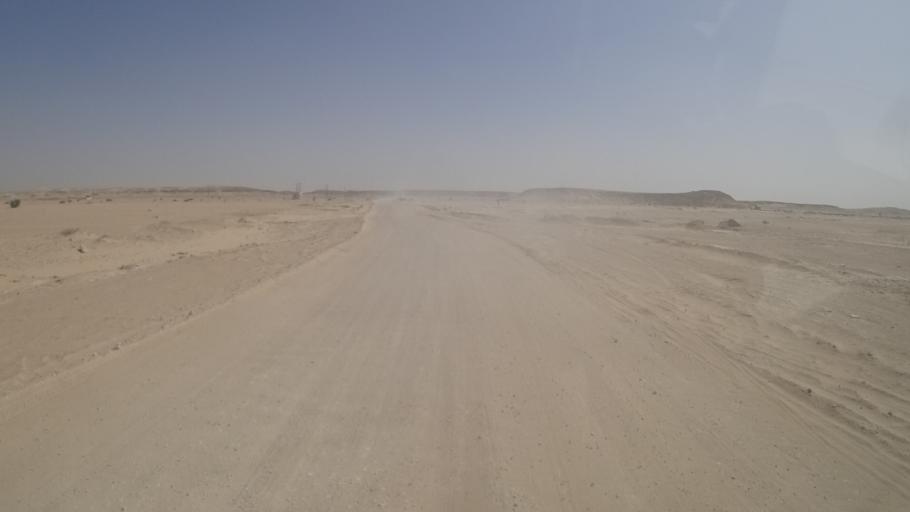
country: YE
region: Al Mahrah
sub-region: Shahan
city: Shihan as Sufla
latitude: 17.8744
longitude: 52.6073
